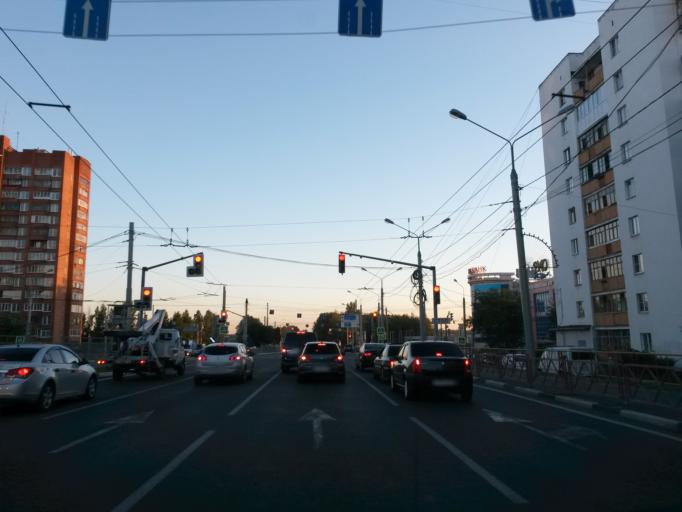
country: RU
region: Jaroslavl
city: Yaroslavl
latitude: 57.5771
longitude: 39.8459
